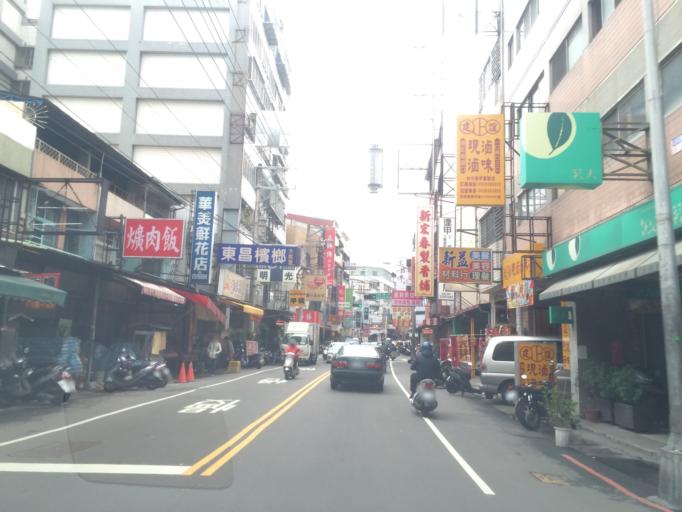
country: TW
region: Taiwan
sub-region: Taichung City
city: Taichung
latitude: 24.1786
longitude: 120.6412
